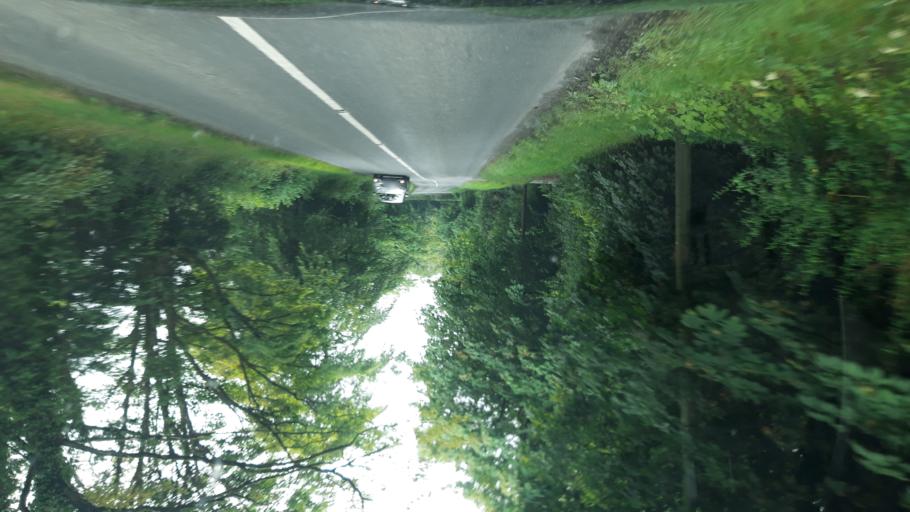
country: IE
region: Munster
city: Fethard
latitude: 52.5393
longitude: -7.6813
